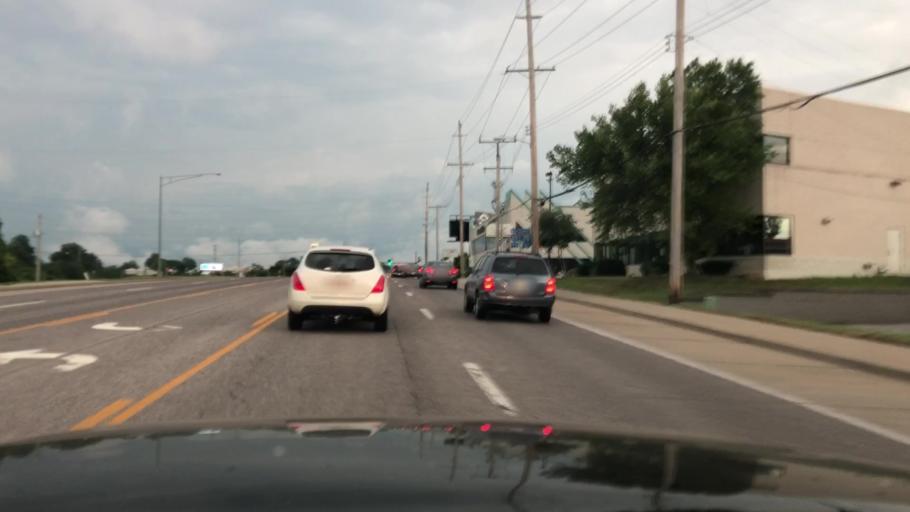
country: US
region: Missouri
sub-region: Saint Louis County
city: Bridgeton
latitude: 38.7451
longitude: -90.4160
